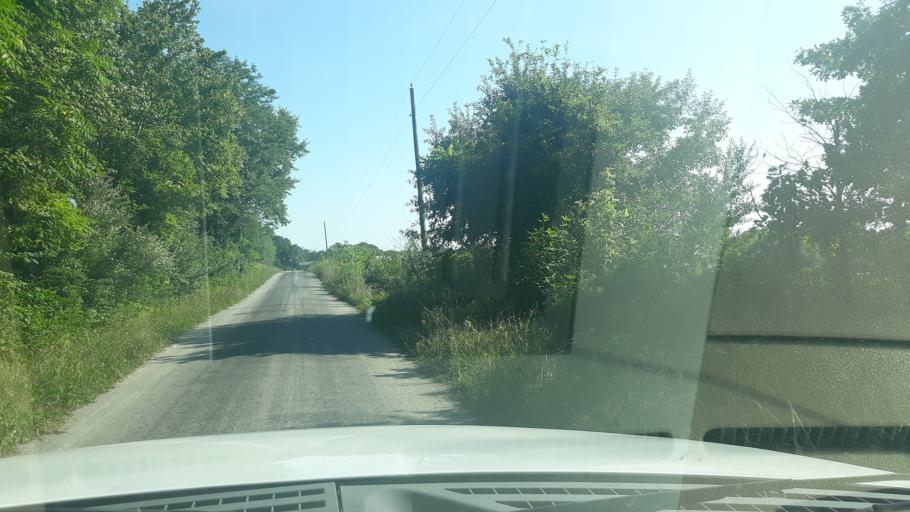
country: US
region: Illinois
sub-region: Saline County
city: Harrisburg
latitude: 37.8511
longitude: -88.6009
